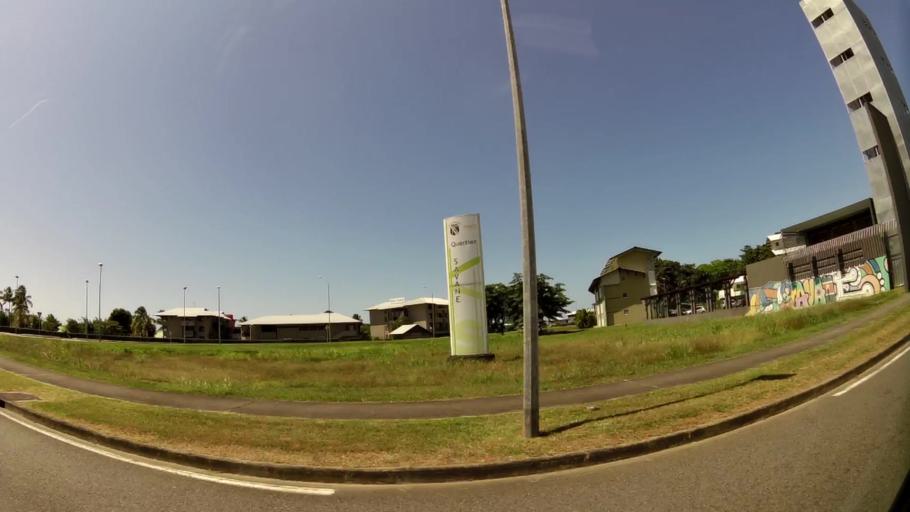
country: GF
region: Guyane
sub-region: Guyane
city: Kourou
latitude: 5.1721
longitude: -52.6575
